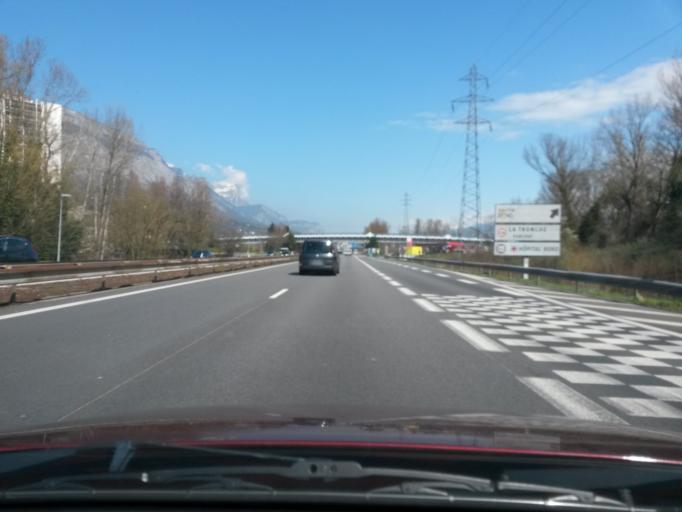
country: FR
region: Rhone-Alpes
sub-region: Departement de l'Isere
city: La Tronche
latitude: 45.1954
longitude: 5.7510
